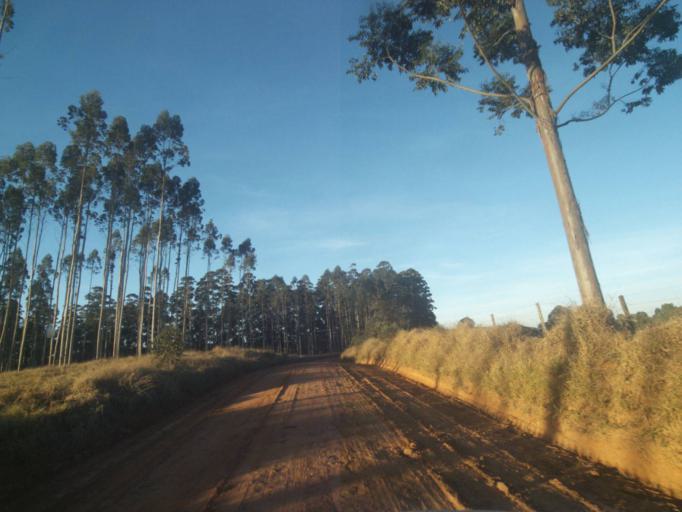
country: BR
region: Parana
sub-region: Tibagi
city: Tibagi
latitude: -24.5533
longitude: -50.5698
